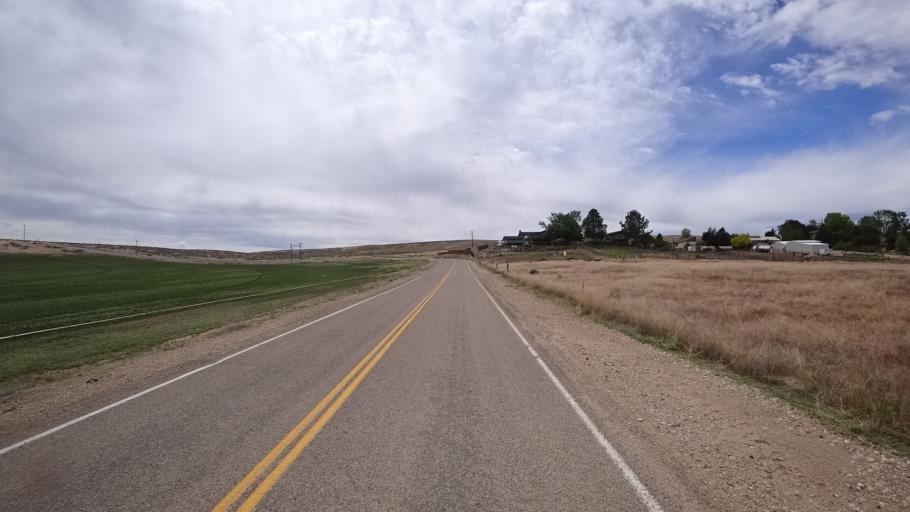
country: US
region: Idaho
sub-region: Ada County
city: Kuna
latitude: 43.4610
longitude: -116.4440
